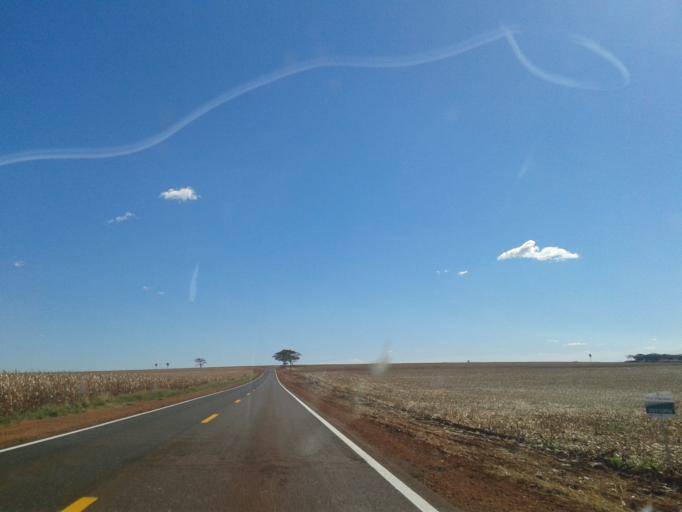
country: BR
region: Minas Gerais
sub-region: Capinopolis
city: Capinopolis
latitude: -18.6927
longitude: -49.4911
